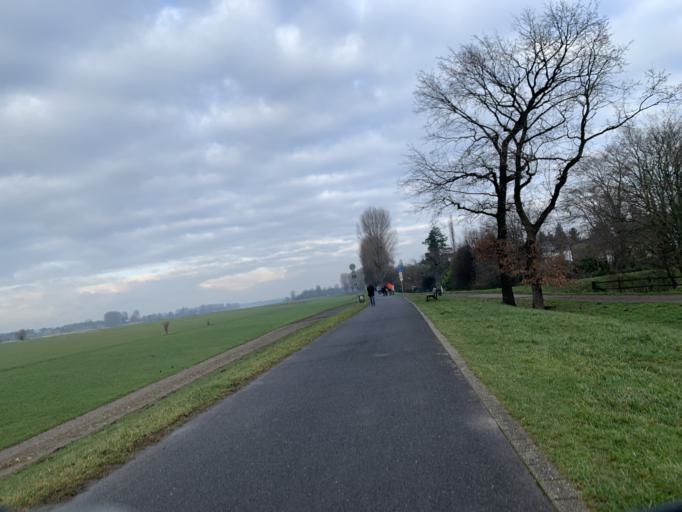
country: DE
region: North Rhine-Westphalia
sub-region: Regierungsbezirk Dusseldorf
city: Meerbusch
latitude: 51.2829
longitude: 6.7211
